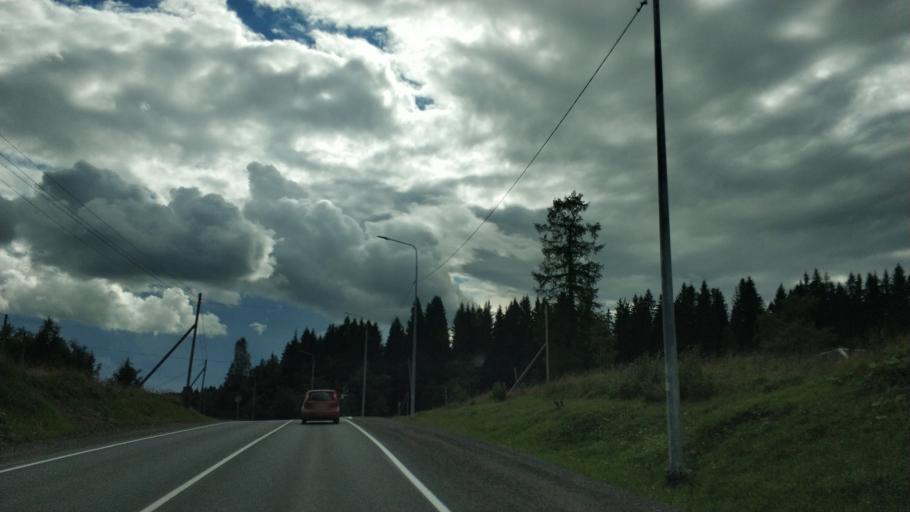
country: RU
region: Republic of Karelia
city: Khelyulya
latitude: 61.7686
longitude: 30.6542
